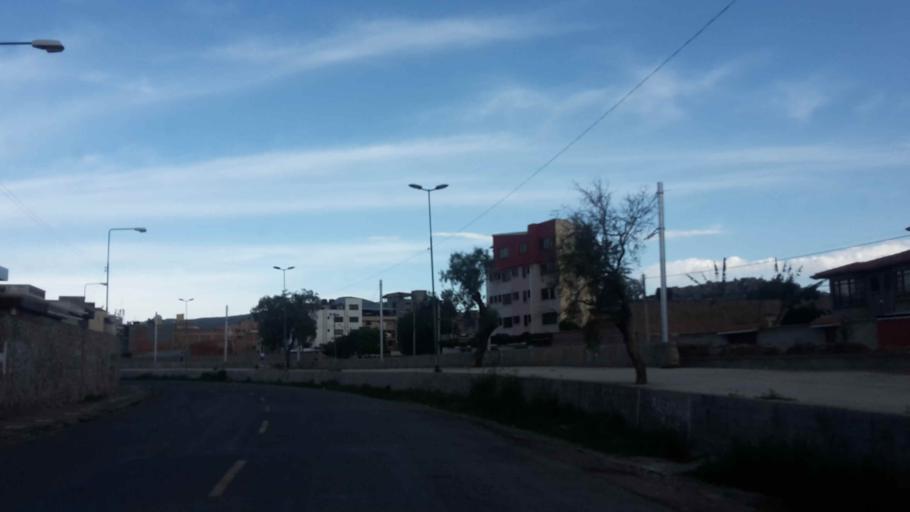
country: BO
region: Cochabamba
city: Cochabamba
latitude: -17.4114
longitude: -66.1599
